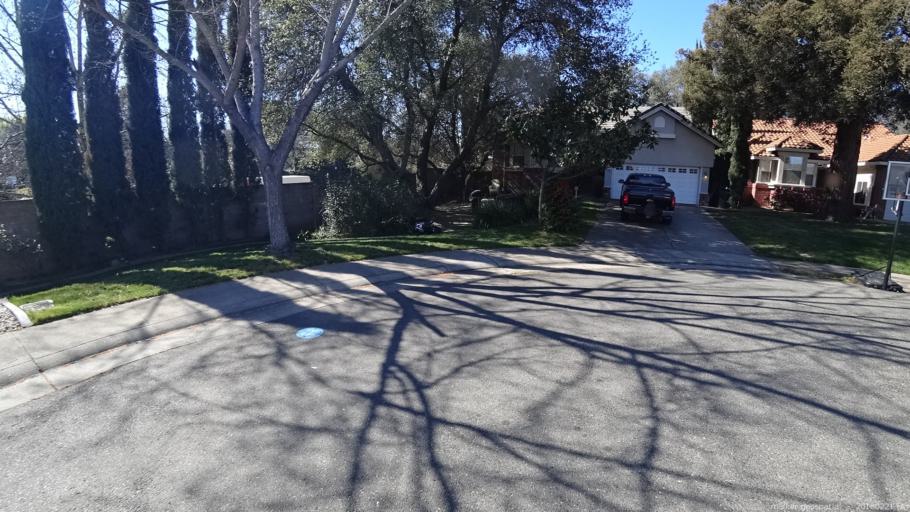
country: US
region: California
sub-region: Sacramento County
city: Orangevale
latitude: 38.6790
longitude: -121.2425
